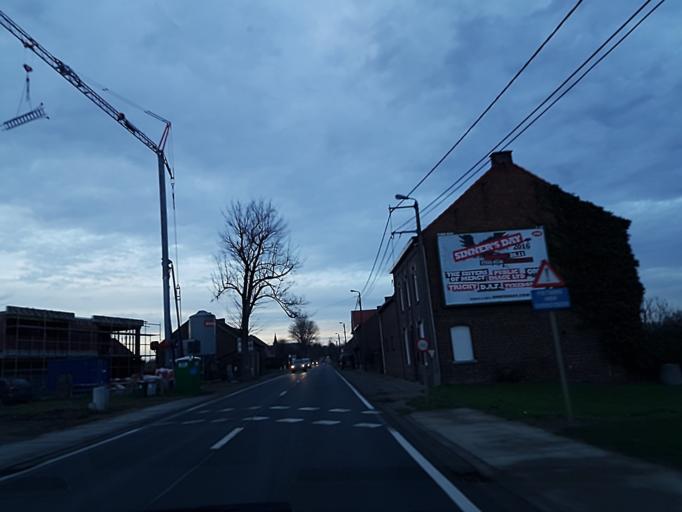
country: BE
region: Flanders
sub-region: Provincie Vlaams-Brabant
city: Lubbeek
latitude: 50.8653
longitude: 4.8902
